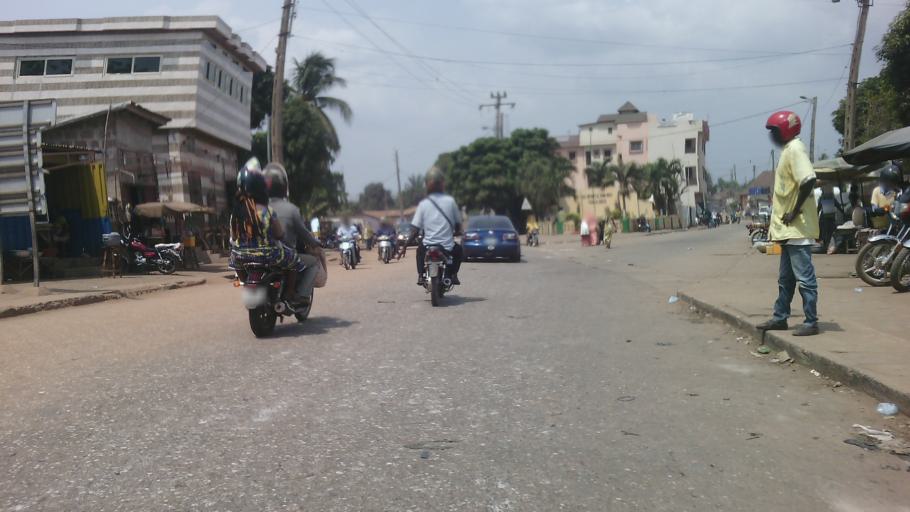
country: BJ
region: Atlantique
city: Abomey-Calavi
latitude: 6.4461
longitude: 2.3539
